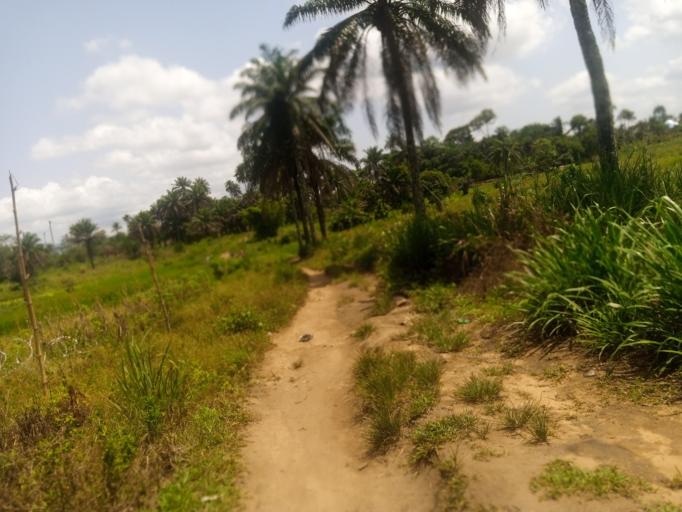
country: SL
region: Western Area
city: Waterloo
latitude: 8.3197
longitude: -13.0091
